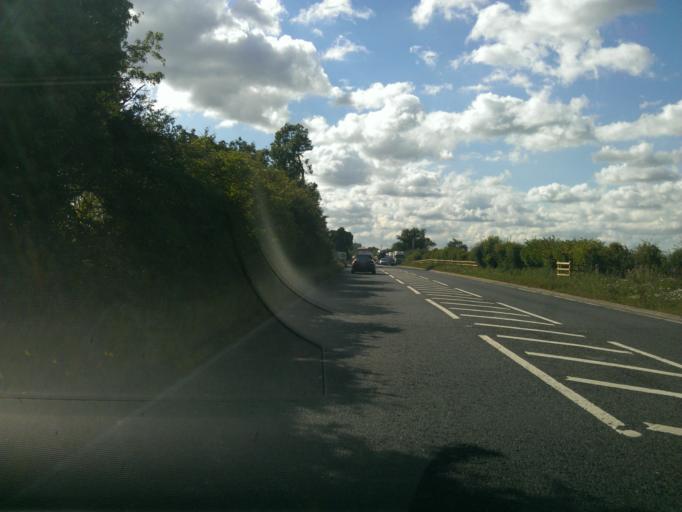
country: GB
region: England
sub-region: Warwickshire
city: Hartshill
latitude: 52.5663
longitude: -1.5091
